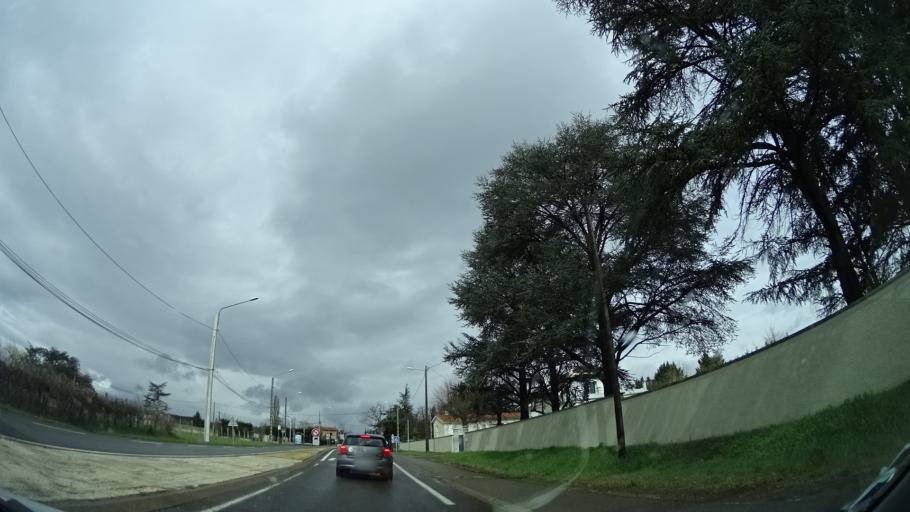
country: FR
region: Rhone-Alpes
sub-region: Departement du Rhone
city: Charbonnieres-les-Bains
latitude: 45.7937
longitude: 4.7416
